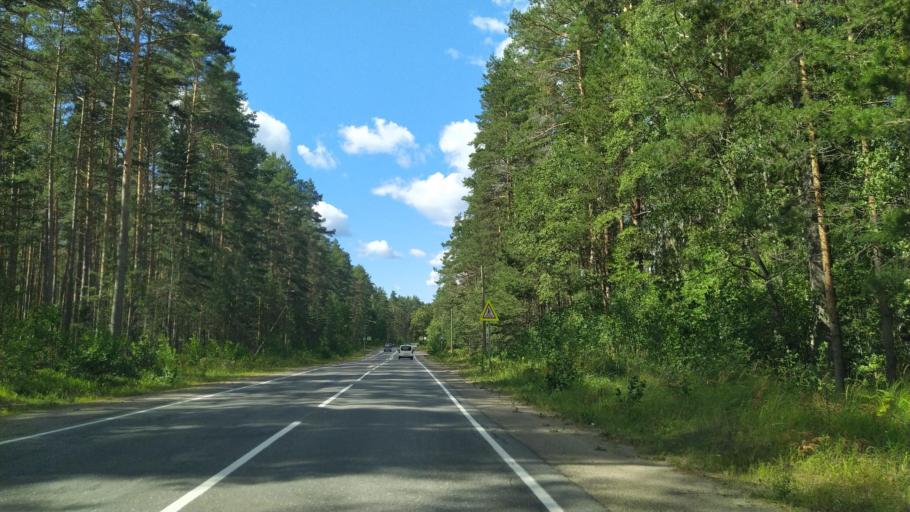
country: RU
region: Leningrad
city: Priozersk
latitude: 61.0029
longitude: 30.2095
